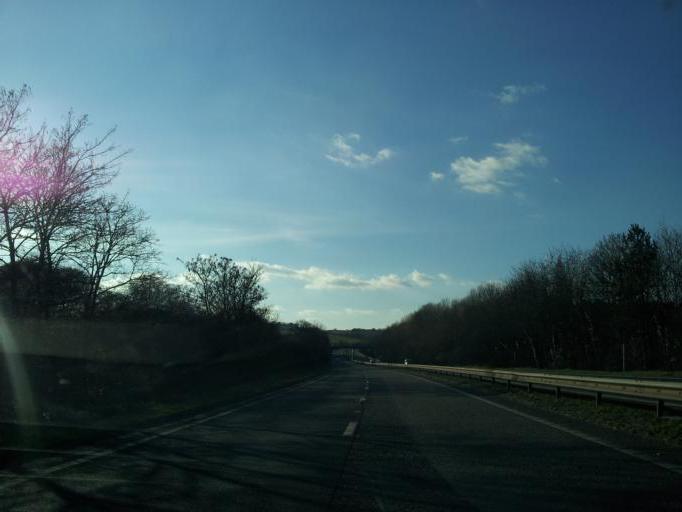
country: GB
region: England
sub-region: Devon
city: Exeter
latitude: 50.7050
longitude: -3.5525
